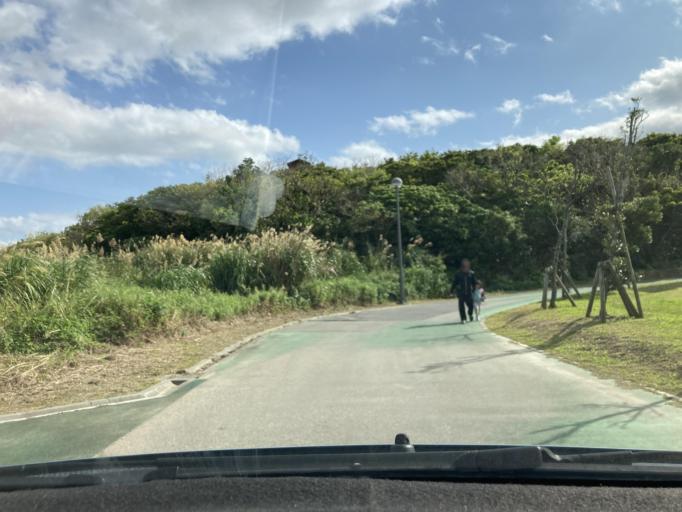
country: JP
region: Okinawa
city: Ginowan
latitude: 26.1867
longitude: 127.7638
